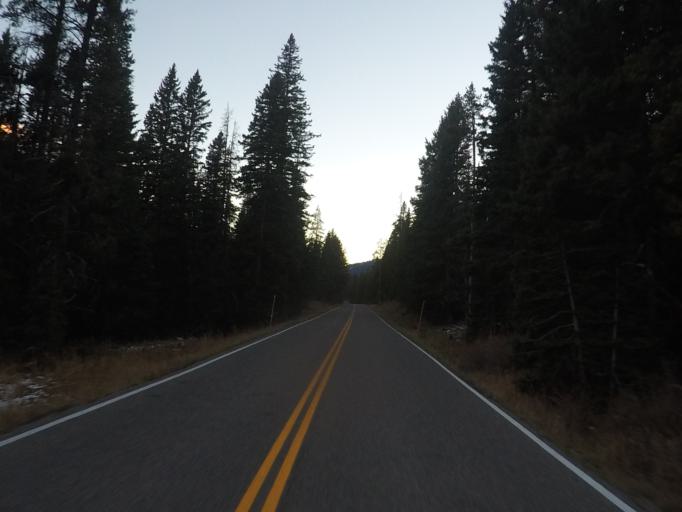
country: US
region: Montana
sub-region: Stillwater County
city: Absarokee
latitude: 45.0017
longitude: -110.0497
